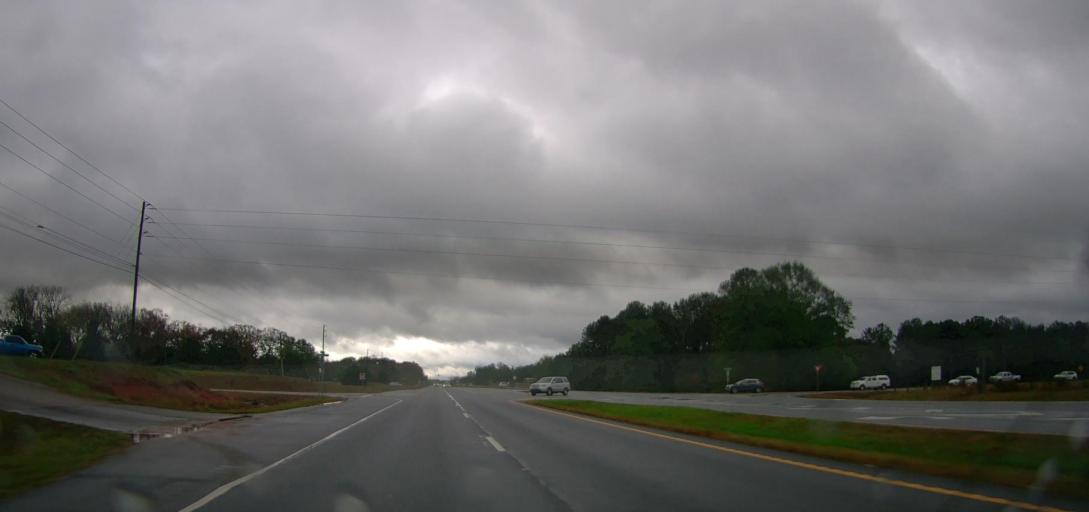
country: US
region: Georgia
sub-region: Jackson County
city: Nicholson
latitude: 34.1493
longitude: -83.4391
